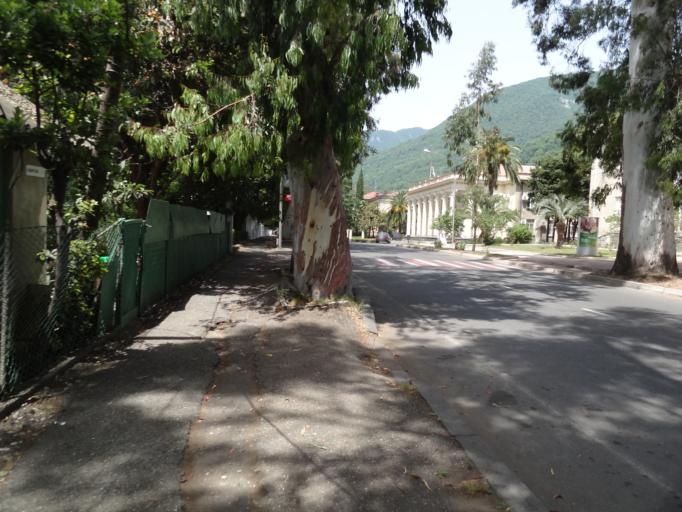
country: GE
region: Abkhazia
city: Gagra
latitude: 43.2957
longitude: 40.2584
